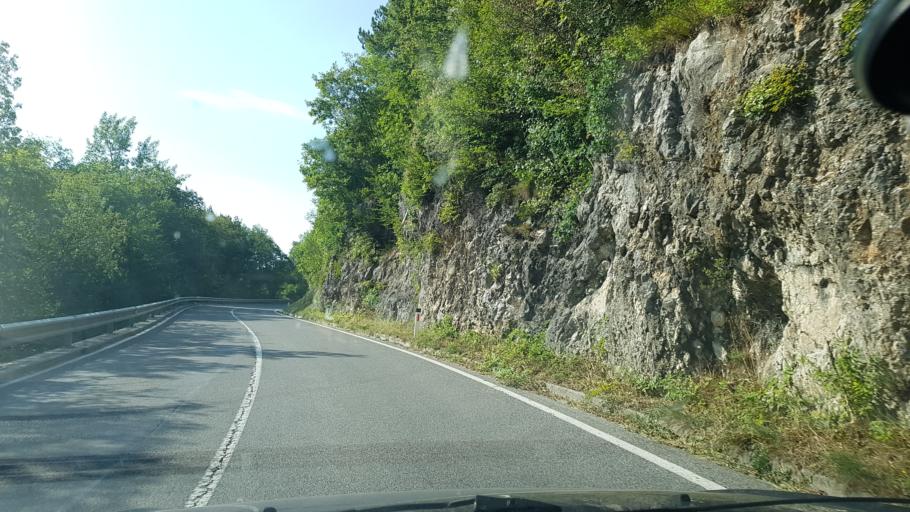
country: SI
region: Nova Gorica
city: Solkan
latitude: 45.9841
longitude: 13.6616
